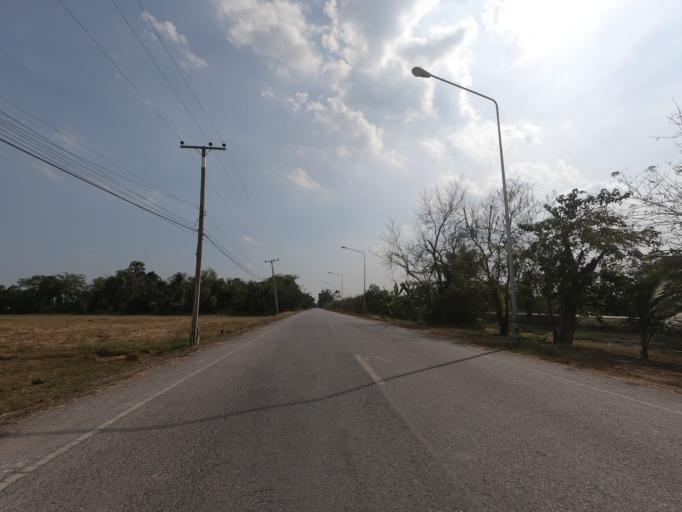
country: TH
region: Pathum Thani
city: Nong Suea
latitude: 14.1264
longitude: 100.8465
